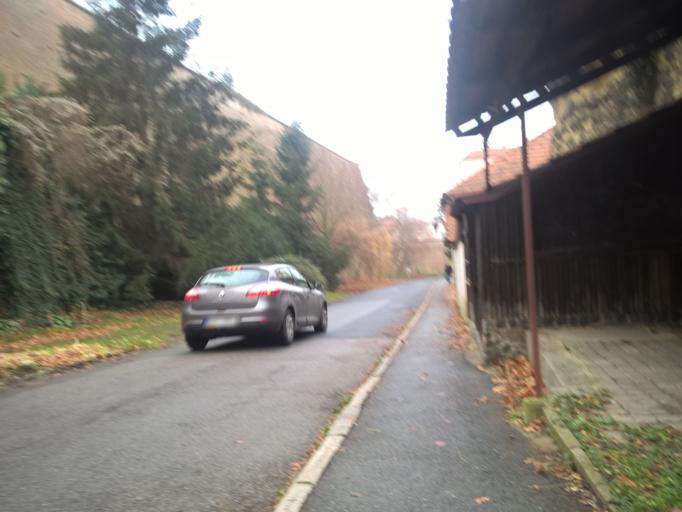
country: CZ
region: Praha
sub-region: Praha 1
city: Mala Strana
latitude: 50.0850
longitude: 14.3882
